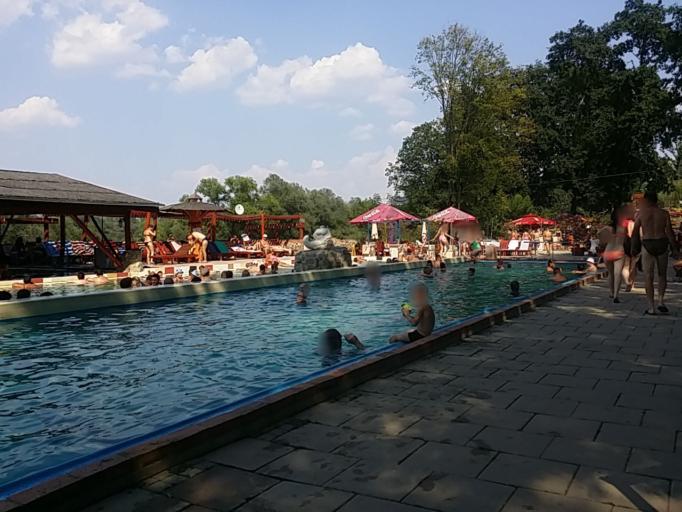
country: HU
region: Baranya
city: Sasd
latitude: 46.1912
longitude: 18.1380
